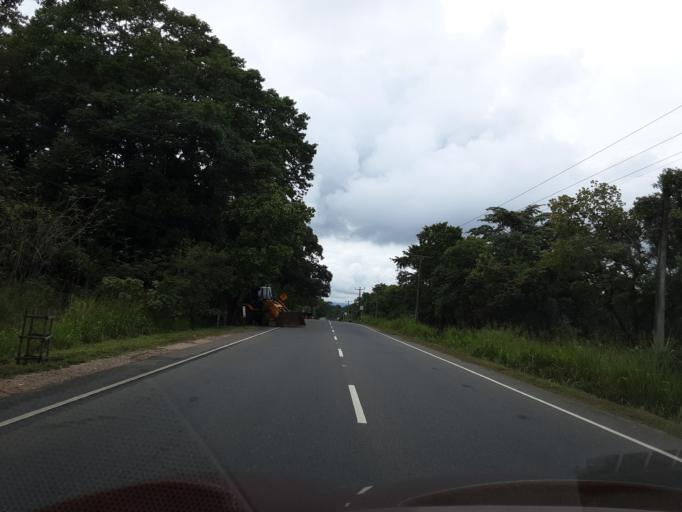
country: LK
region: Uva
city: Badulla
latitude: 7.3983
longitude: 81.1091
